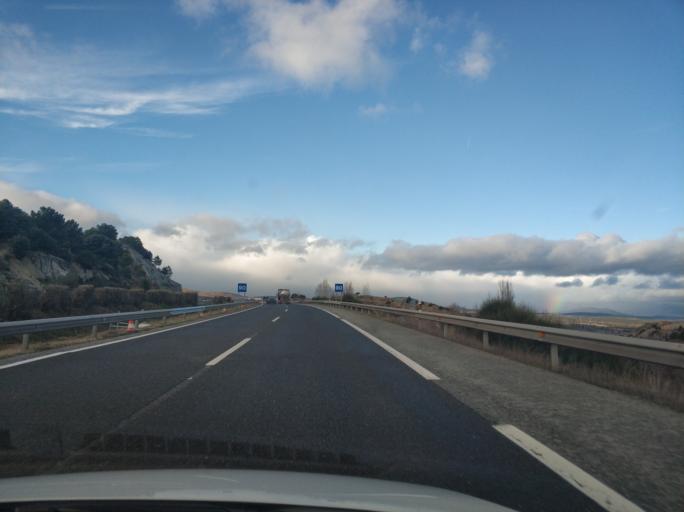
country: ES
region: Madrid
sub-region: Provincia de Madrid
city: La Cabrera
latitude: 40.8875
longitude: -3.5990
